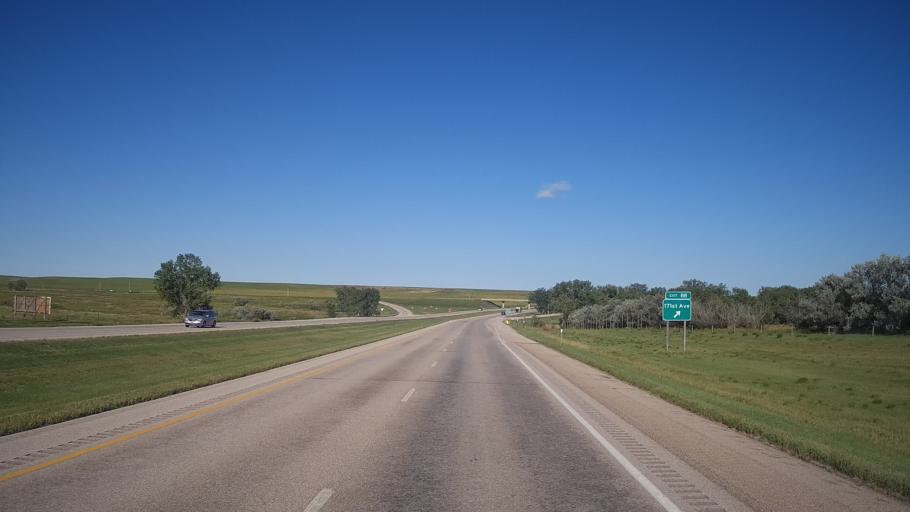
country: US
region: South Dakota
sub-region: Pennington County
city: Box Elder
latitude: 44.1052
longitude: -102.6362
